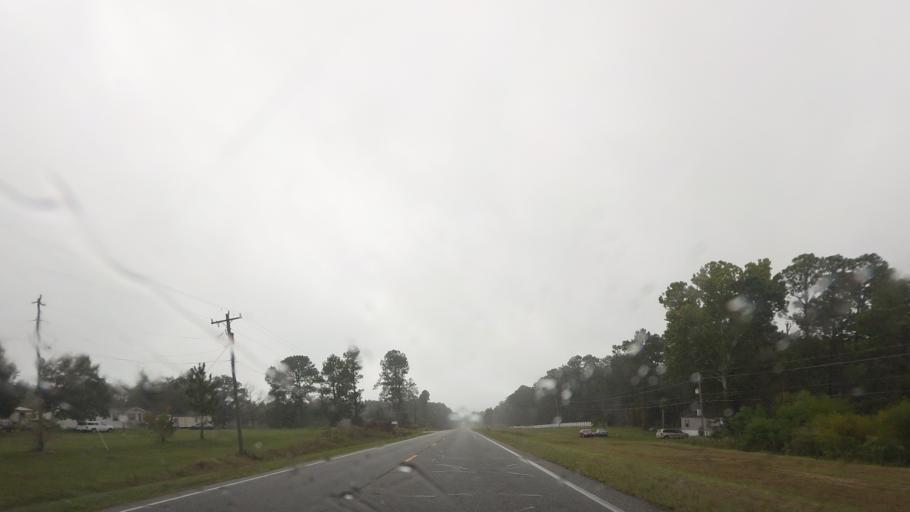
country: US
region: Georgia
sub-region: Ben Hill County
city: Fitzgerald
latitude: 31.7552
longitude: -83.2458
